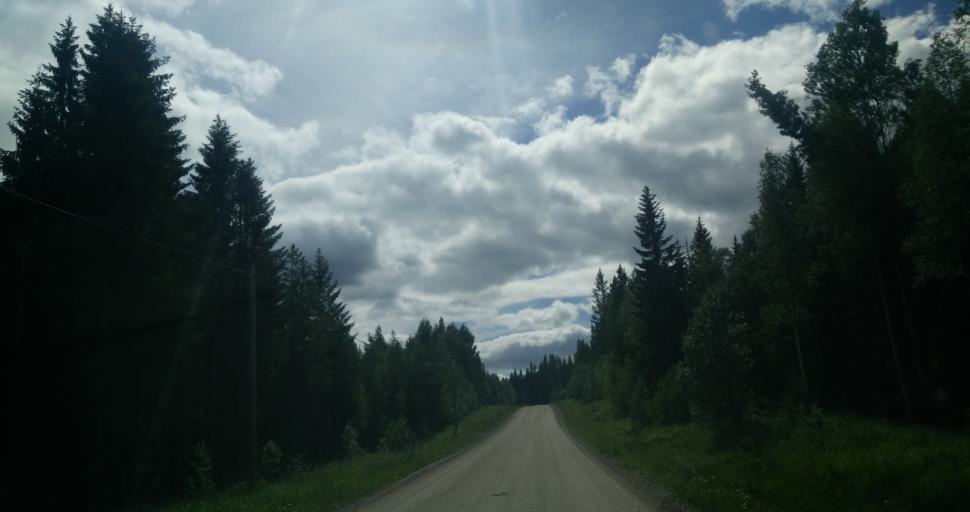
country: SE
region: Vaesternorrland
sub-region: Sundsvalls Kommun
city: Vi
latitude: 62.1392
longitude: 17.1323
